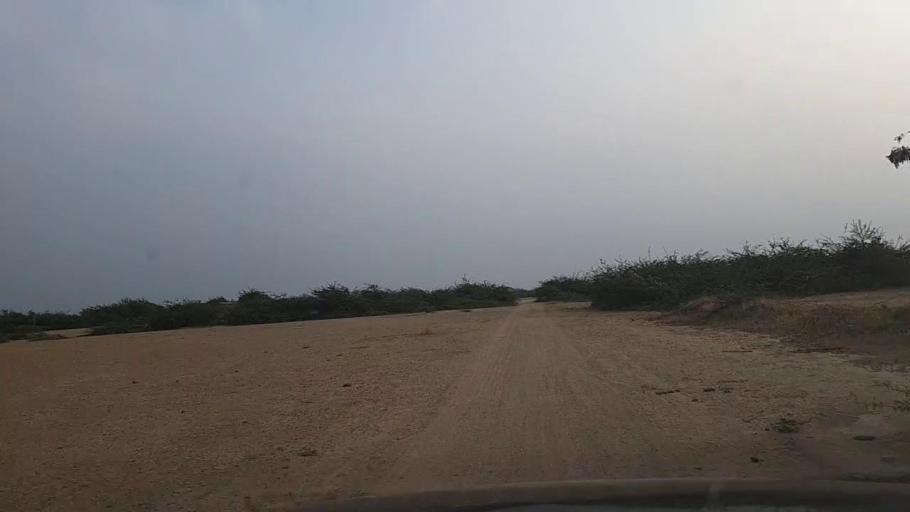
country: PK
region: Sindh
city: Gharo
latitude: 24.7761
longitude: 67.7070
